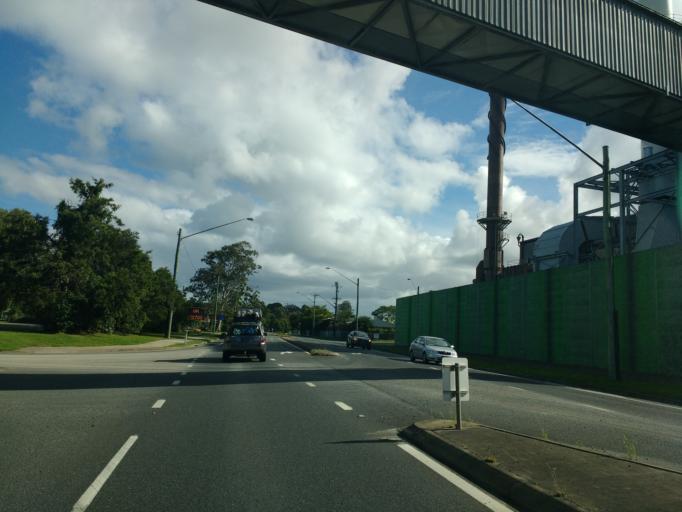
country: AU
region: New South Wales
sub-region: Richmond Valley
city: Evans Head
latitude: -29.0119
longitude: 153.4344
